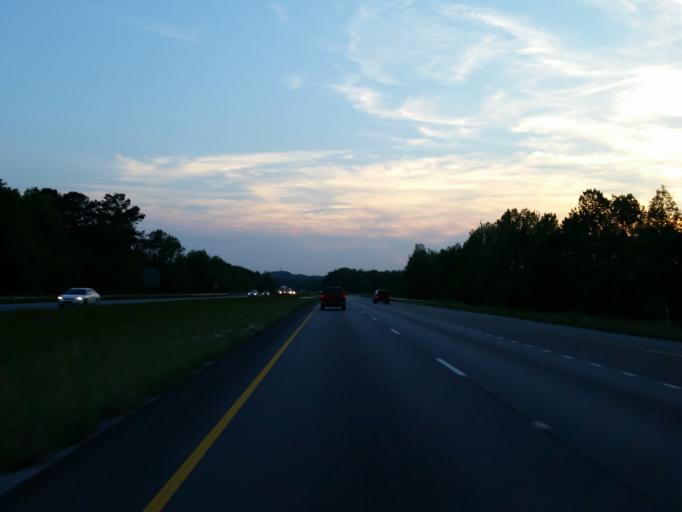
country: US
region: Alabama
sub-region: Calhoun County
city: Choccolocco
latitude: 33.6176
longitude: -85.7268
